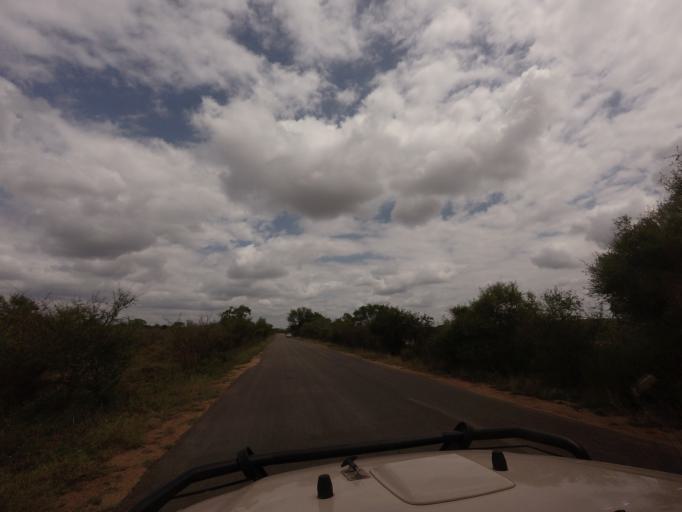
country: ZA
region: Mpumalanga
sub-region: Ehlanzeni District
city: Komatipoort
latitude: -25.0978
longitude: 31.8795
